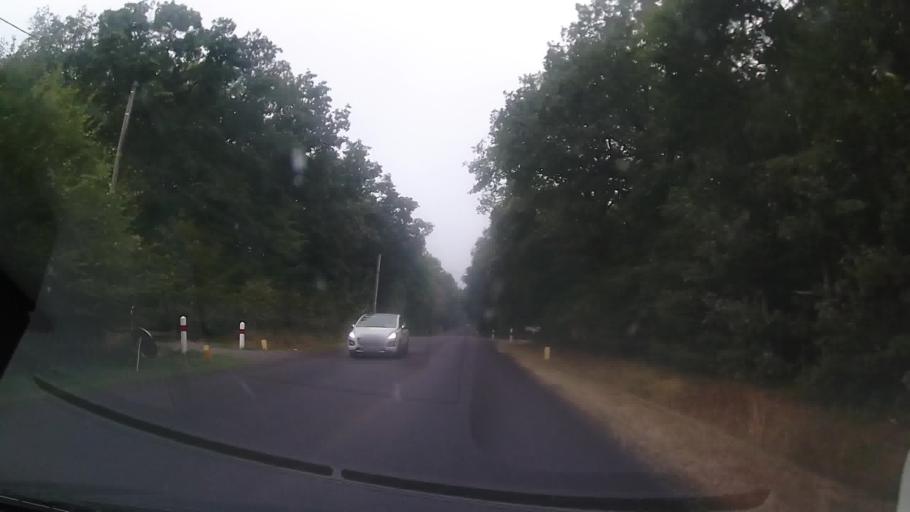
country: FR
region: Ile-de-France
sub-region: Departement de l'Essonne
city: Dourdan
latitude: 48.5429
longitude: 1.9962
